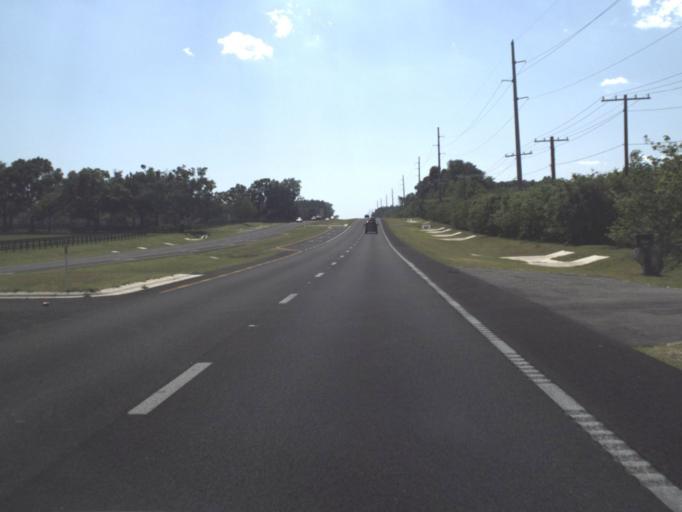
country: US
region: Florida
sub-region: Marion County
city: Ocala
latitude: 29.1869
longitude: -82.2643
